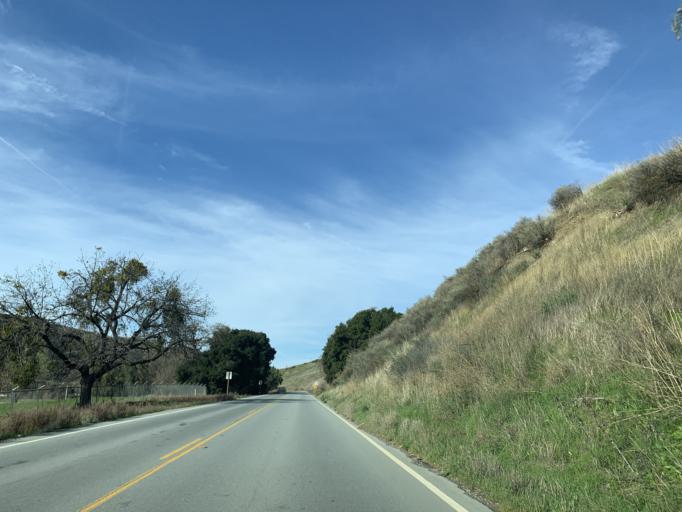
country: US
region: California
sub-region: San Benito County
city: Ridgemark
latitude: 36.7695
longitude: -121.3038
